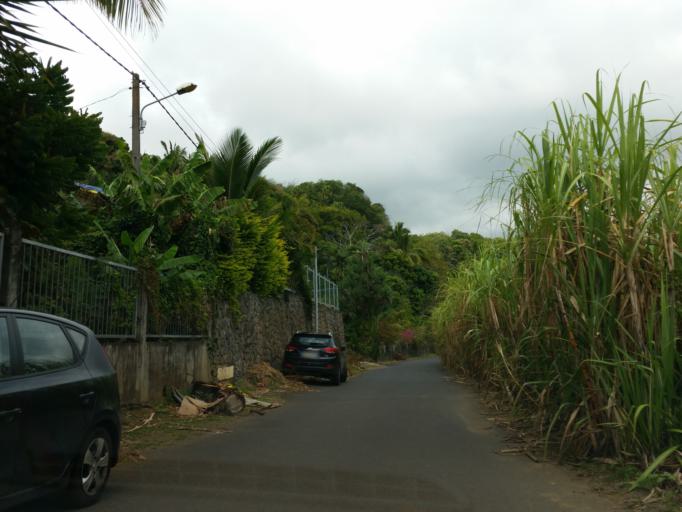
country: RE
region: Reunion
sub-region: Reunion
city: Sainte-Suzanne
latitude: -20.9184
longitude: 55.6128
